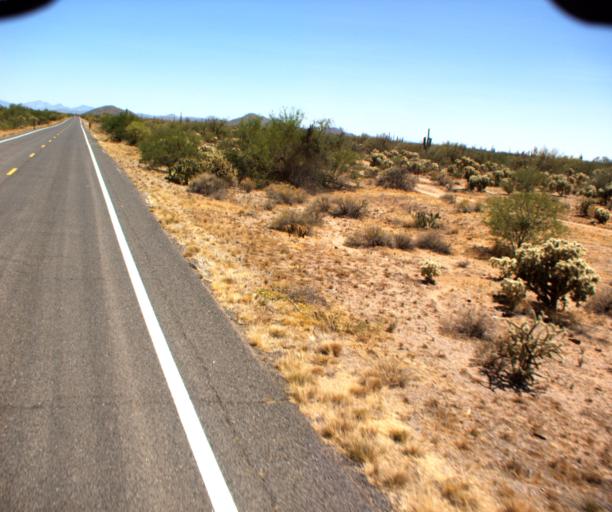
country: US
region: Arizona
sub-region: Pinal County
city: Florence
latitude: 32.7884
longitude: -111.1722
